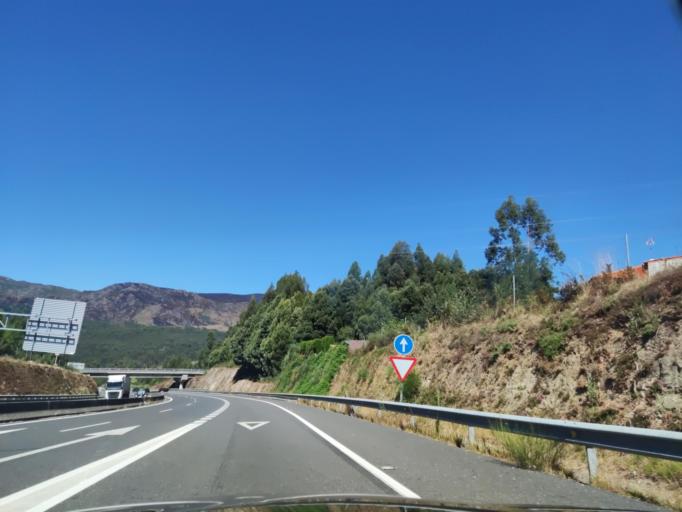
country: ES
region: Galicia
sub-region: Provincia da Coruna
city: Boiro
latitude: 42.6592
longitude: -8.8843
